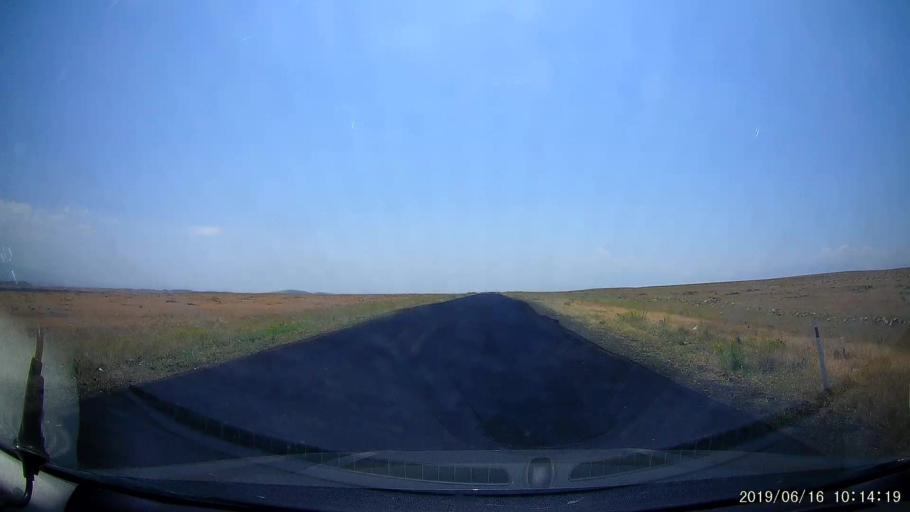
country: TR
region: Igdir
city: Tuzluca
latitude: 40.1859
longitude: 43.6602
